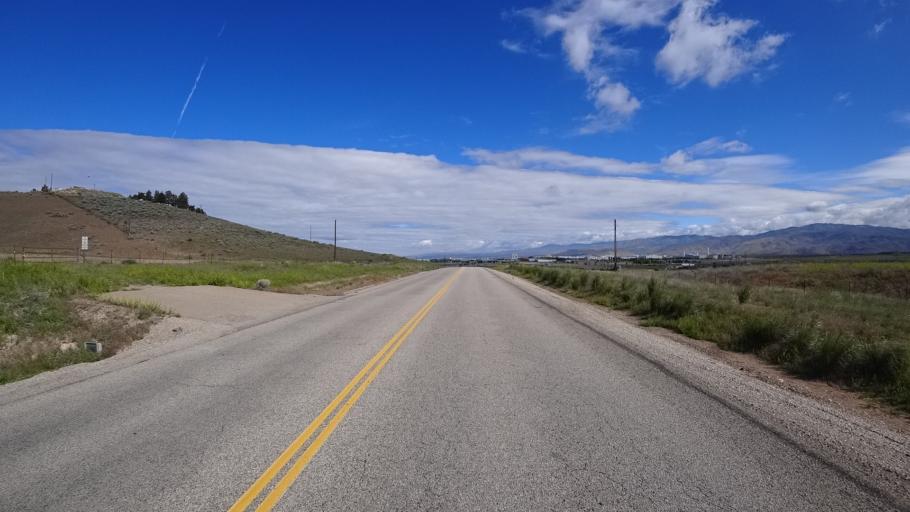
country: US
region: Idaho
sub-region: Ada County
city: Boise
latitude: 43.5088
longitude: -116.1475
